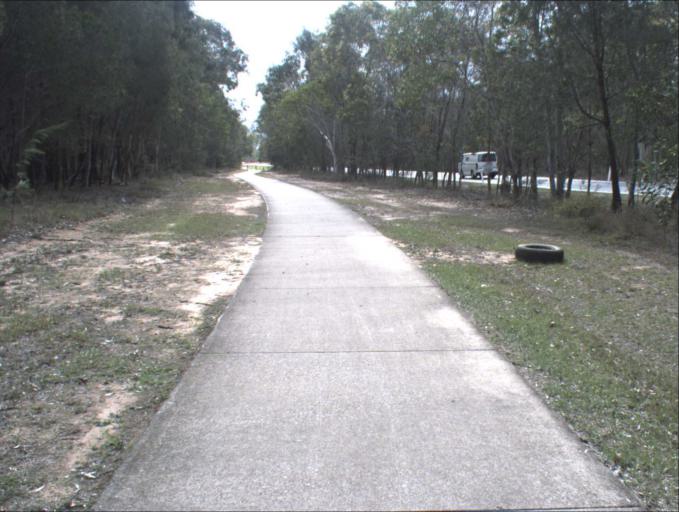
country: AU
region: Queensland
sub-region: Logan
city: Logan Reserve
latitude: -27.6772
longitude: 153.0694
